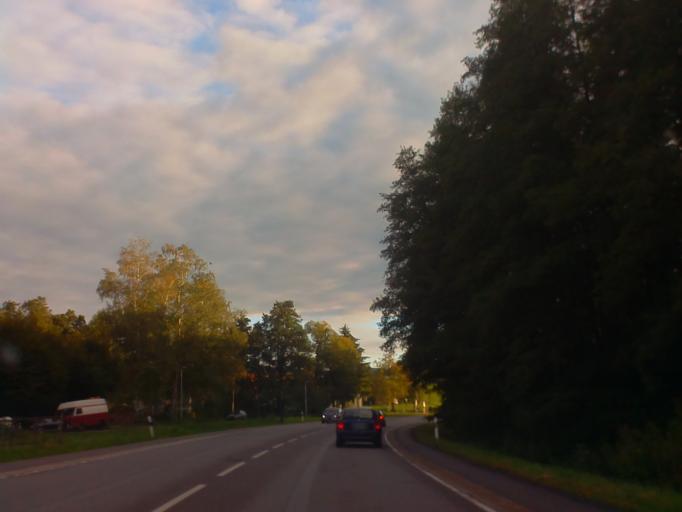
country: DE
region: Hesse
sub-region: Regierungsbezirk Darmstadt
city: Rimbach
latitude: 49.6116
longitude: 8.7536
